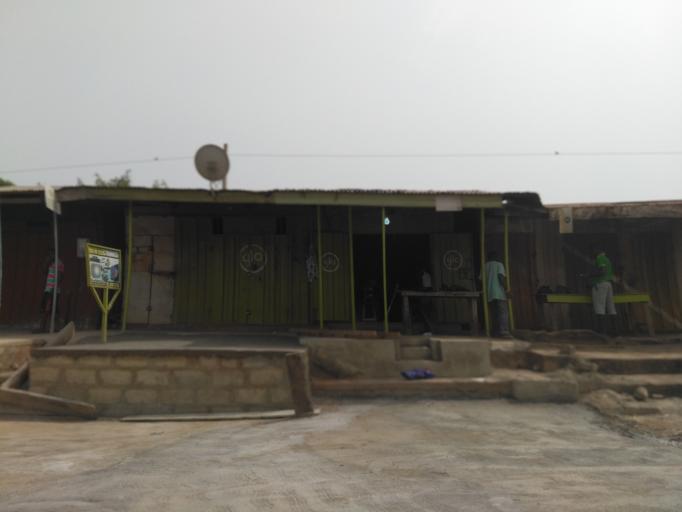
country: GH
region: Ashanti
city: Kumasi
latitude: 6.6427
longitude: -1.6450
